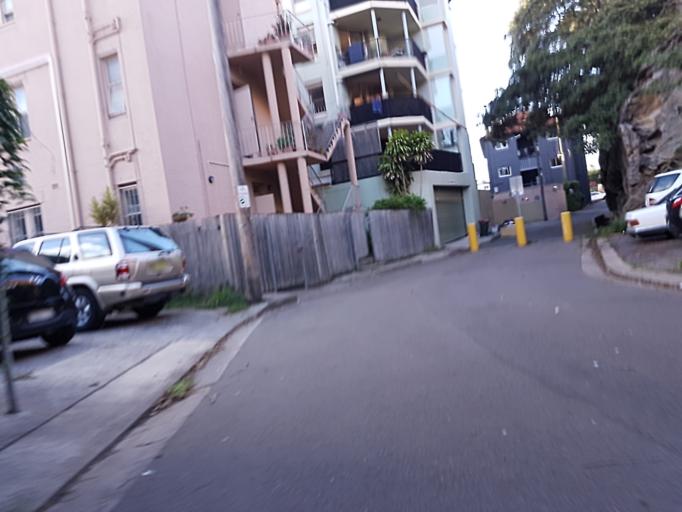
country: AU
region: New South Wales
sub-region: Manly Vale
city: Manly
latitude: -33.7946
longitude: 151.2847
